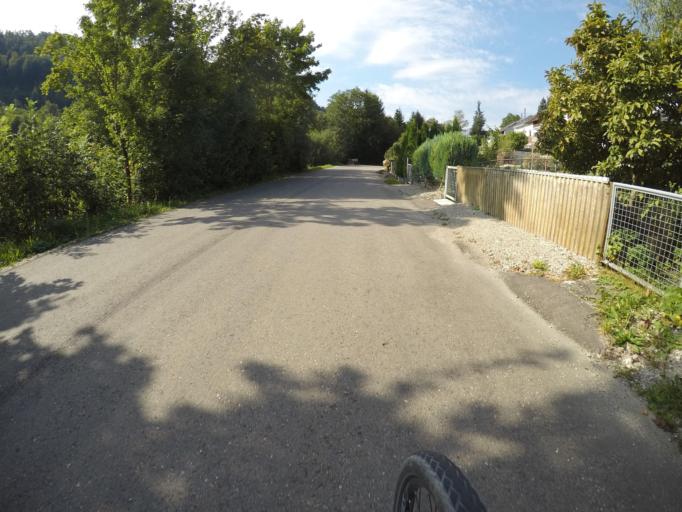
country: DE
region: Baden-Wuerttemberg
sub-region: Regierungsbezirk Stuttgart
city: Geislingen an der Steige
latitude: 48.6343
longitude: 9.8604
